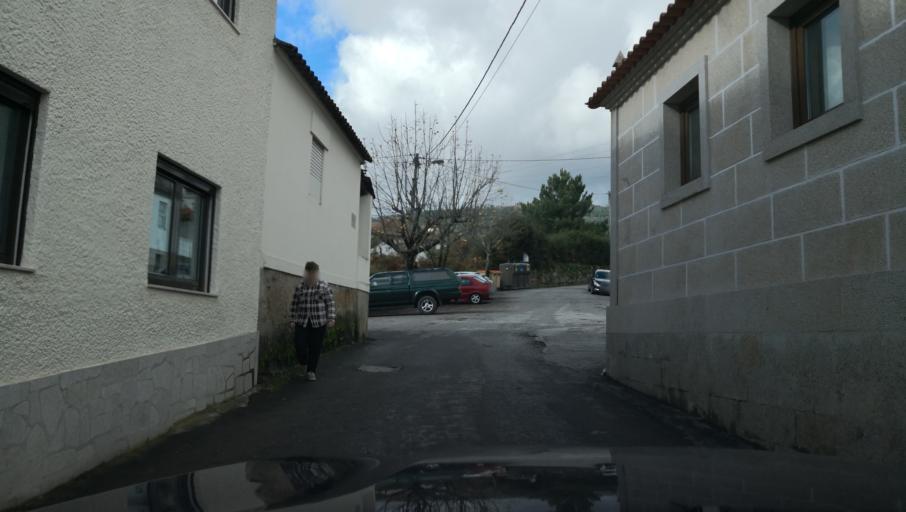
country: PT
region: Vila Real
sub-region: Vila Real
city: Vila Real
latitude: 41.3197
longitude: -7.7610
